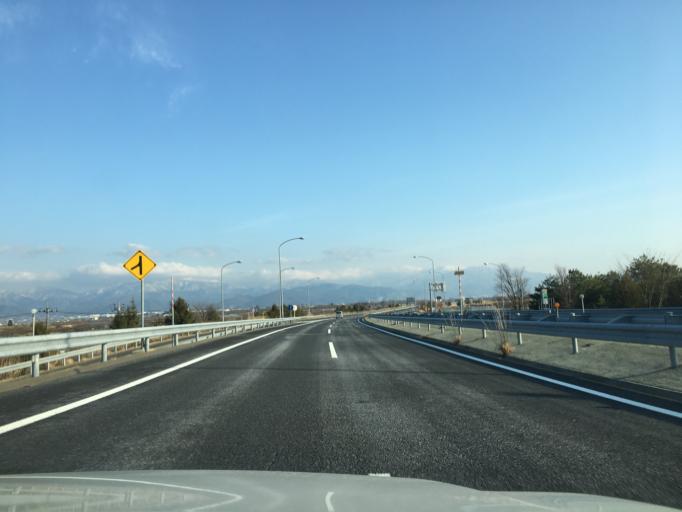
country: JP
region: Yamagata
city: Sagae
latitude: 38.3580
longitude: 140.2926
